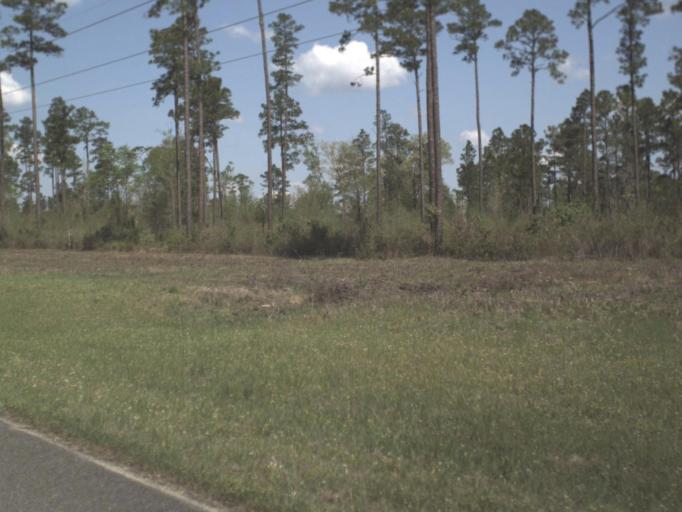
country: US
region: Florida
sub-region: Santa Rosa County
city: Point Baker
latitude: 30.8763
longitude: -86.9446
